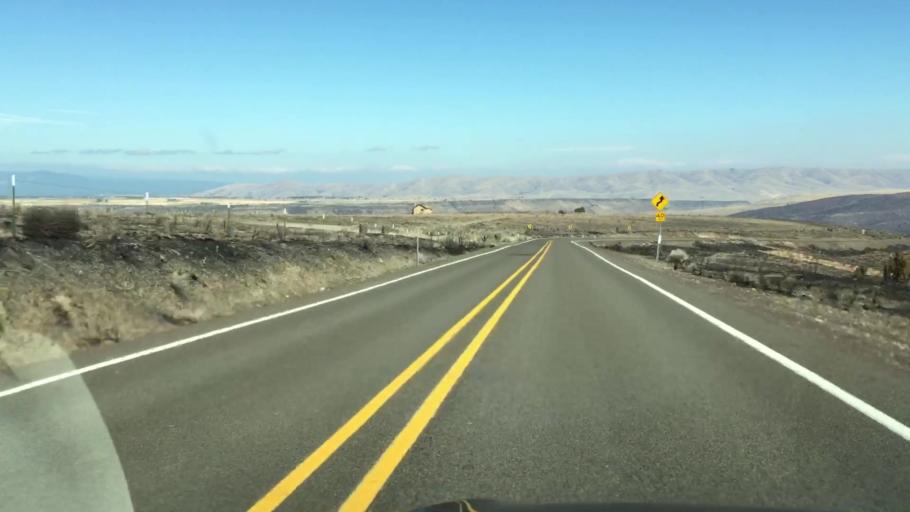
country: US
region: Oregon
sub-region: Jefferson County
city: Warm Springs
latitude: 45.1347
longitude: -121.0513
